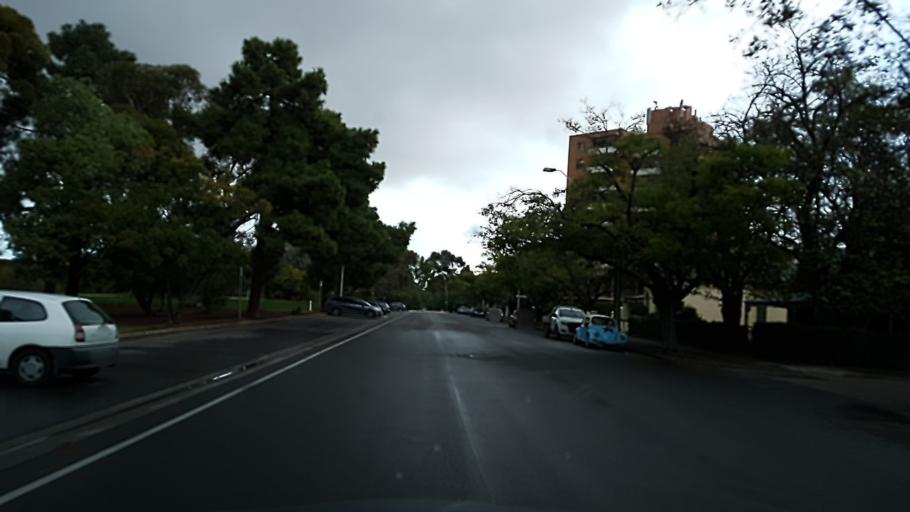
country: AU
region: South Australia
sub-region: Adelaide
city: North Adelaide
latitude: -34.9112
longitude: 138.5855
